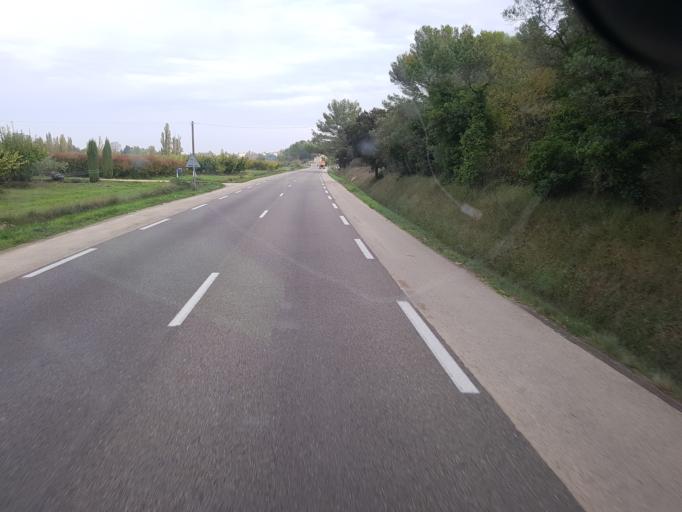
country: FR
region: Provence-Alpes-Cote d'Azur
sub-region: Departement des Bouches-du-Rhone
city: Barbentane
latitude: 43.8995
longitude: 4.7255
